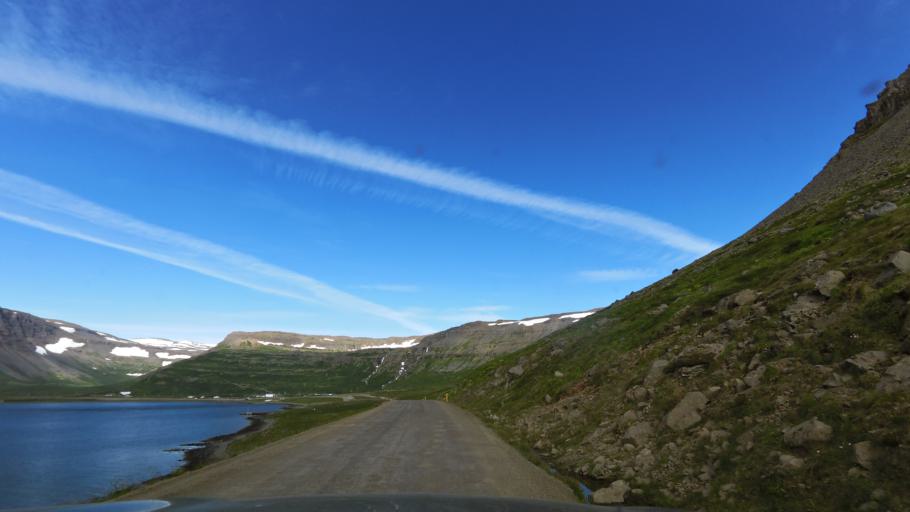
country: IS
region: Westfjords
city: Isafjoerdur
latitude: 65.7656
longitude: -23.1940
